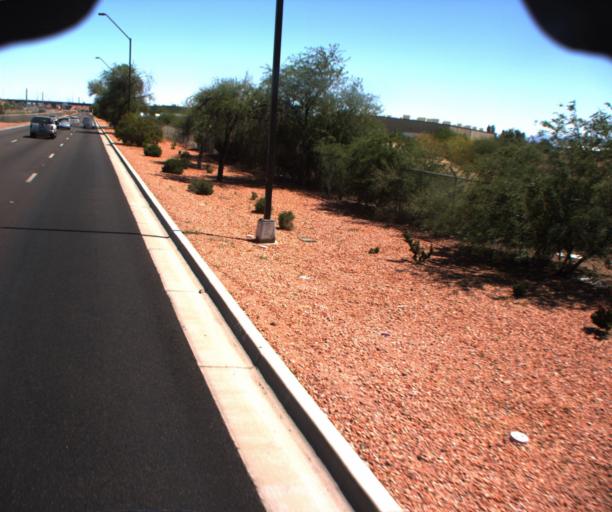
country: US
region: Arizona
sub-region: Maricopa County
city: Peoria
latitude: 33.5721
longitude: -112.2266
